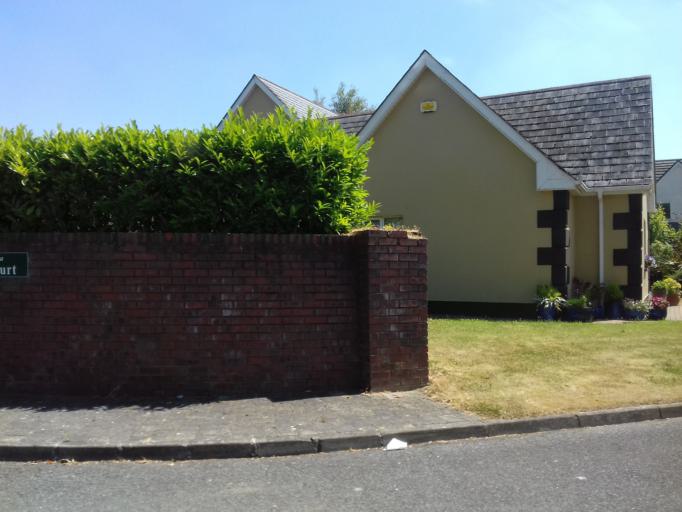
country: IE
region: Leinster
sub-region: An Mhi
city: Ashbourne
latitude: 53.5242
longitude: -6.3168
